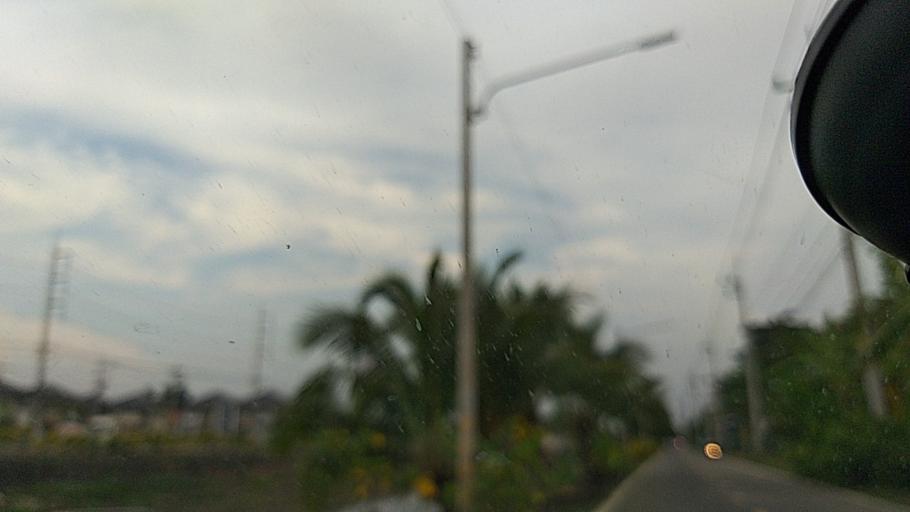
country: TH
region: Pathum Thani
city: Thanyaburi
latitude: 14.0660
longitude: 100.7098
